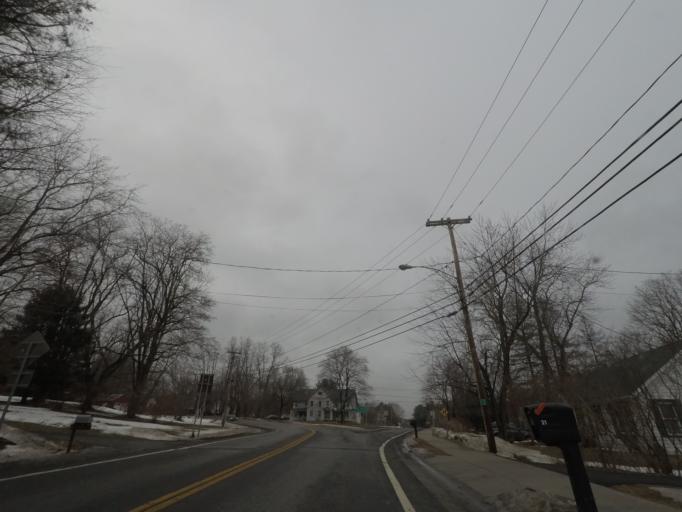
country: US
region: New York
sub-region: Albany County
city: Voorheesville
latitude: 42.6515
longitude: -73.9380
